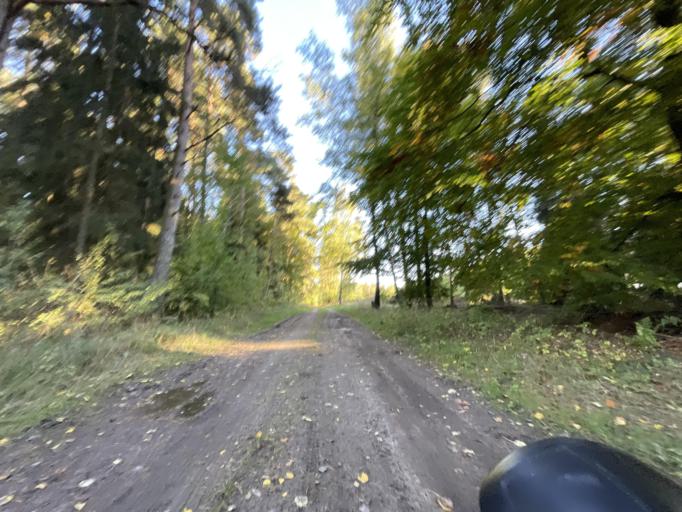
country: DE
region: Lower Saxony
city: Vastorf
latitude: 53.1991
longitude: 10.5187
